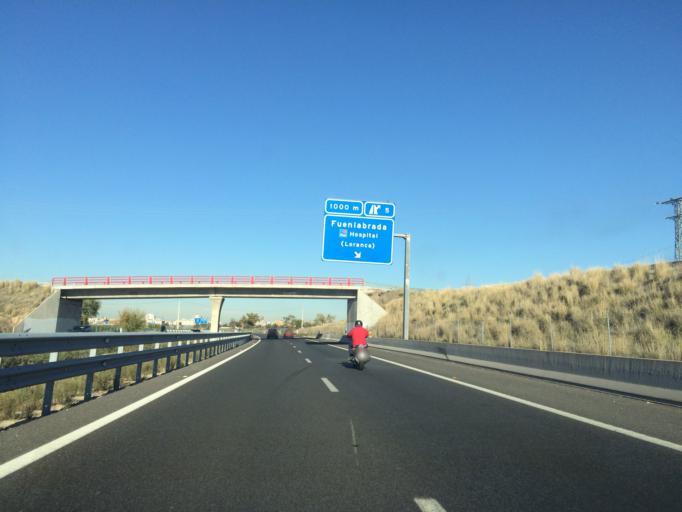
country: ES
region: Madrid
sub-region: Provincia de Madrid
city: Humanes de Madrid
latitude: 40.2807
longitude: -3.8352
